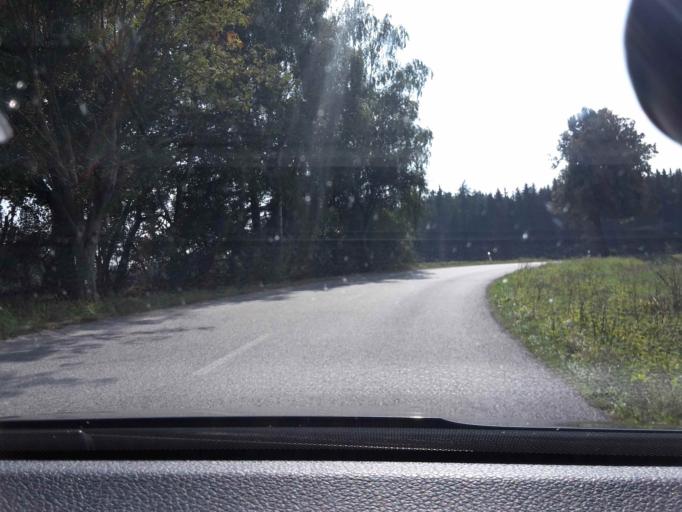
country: CZ
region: Vysocina
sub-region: Okres Jihlava
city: Trest'
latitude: 49.2635
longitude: 15.5734
